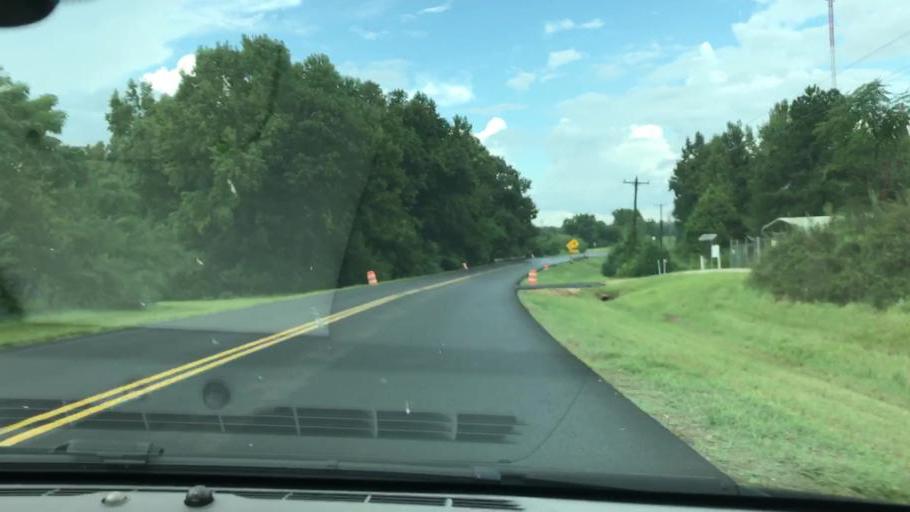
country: US
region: Georgia
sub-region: Early County
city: Blakely
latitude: 31.4002
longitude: -84.9579
